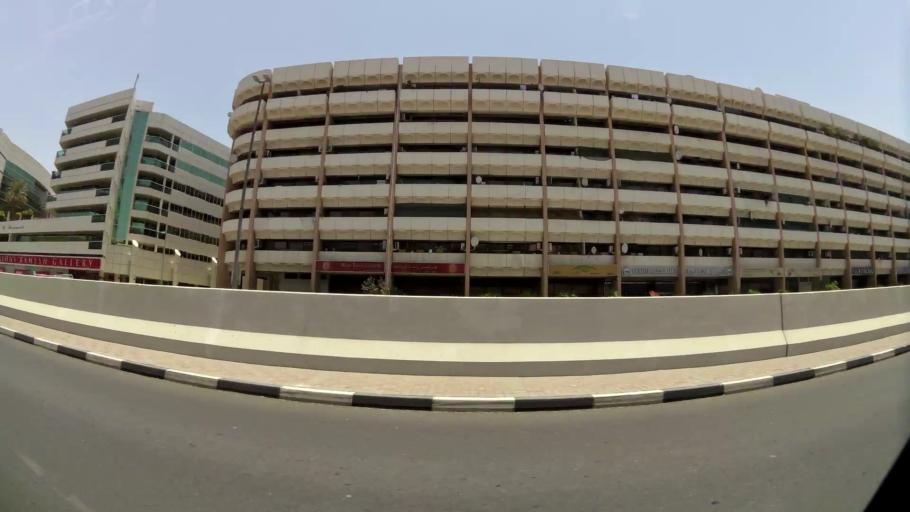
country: AE
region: Ash Shariqah
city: Sharjah
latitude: 25.2414
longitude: 55.3063
